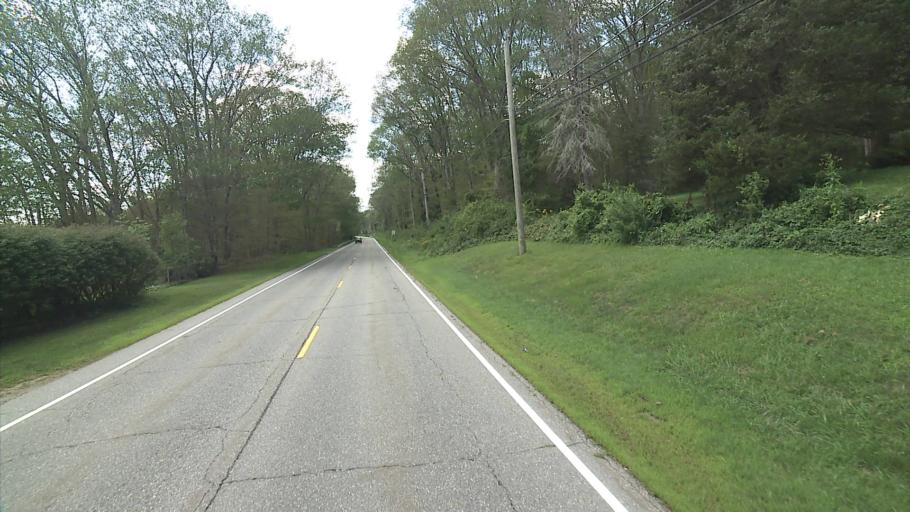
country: US
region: Connecticut
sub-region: Windham County
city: Windham
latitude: 41.8089
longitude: -72.1170
